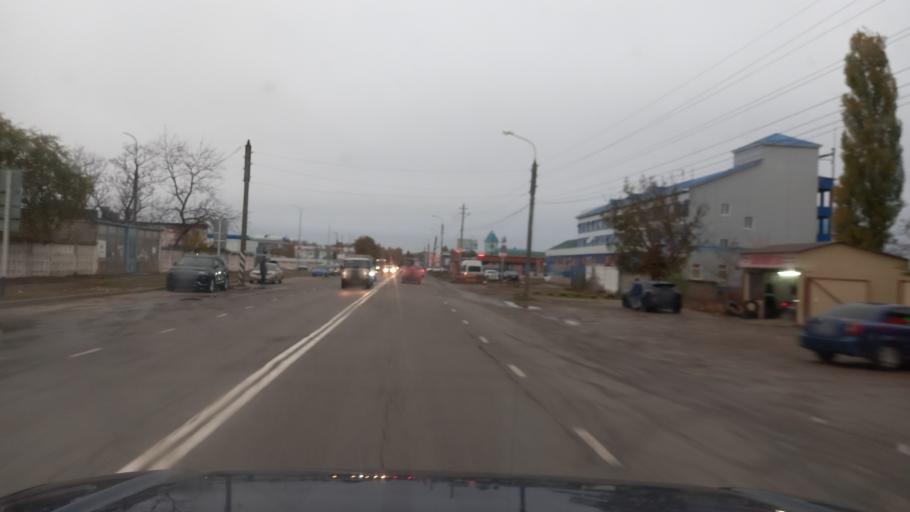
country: RU
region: Adygeya
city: Maykop
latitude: 44.6223
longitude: 40.0632
